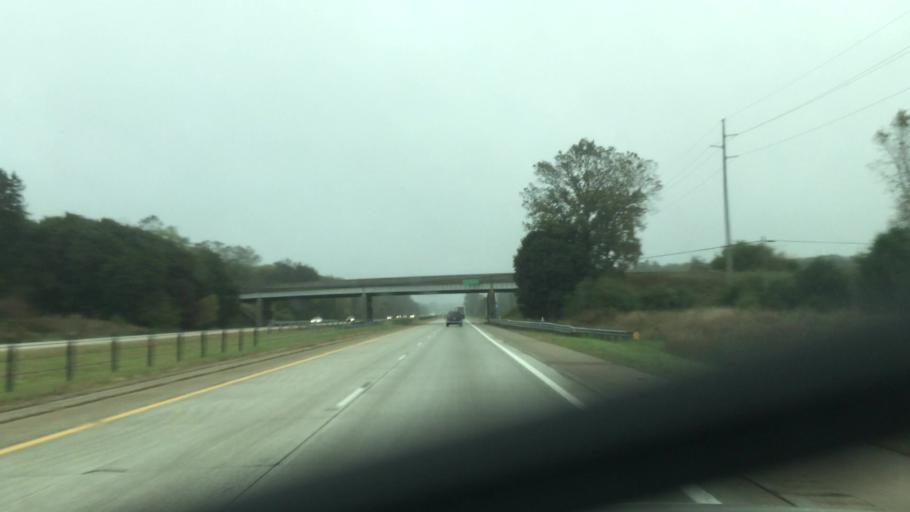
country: US
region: Michigan
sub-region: Van Buren County
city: Paw Paw
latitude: 42.2051
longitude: -85.9136
